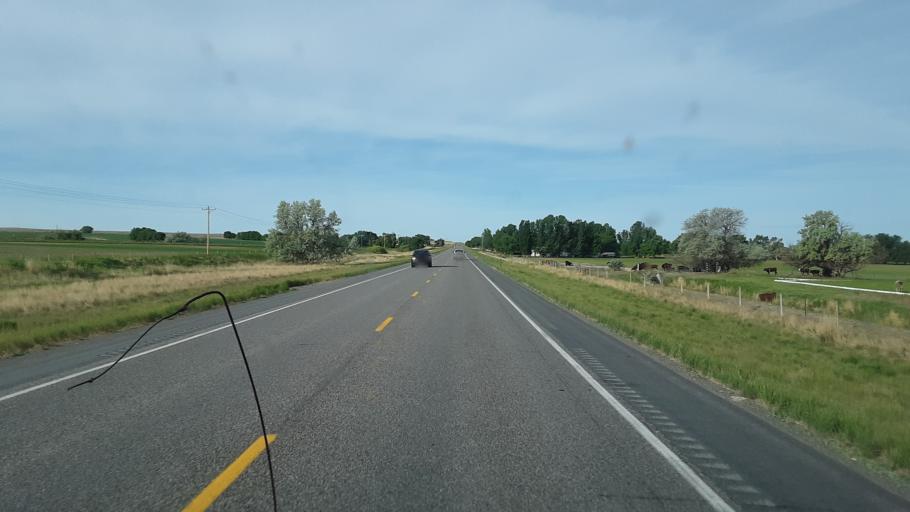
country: US
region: Wyoming
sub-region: Fremont County
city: Riverton
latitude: 43.1799
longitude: -108.2511
